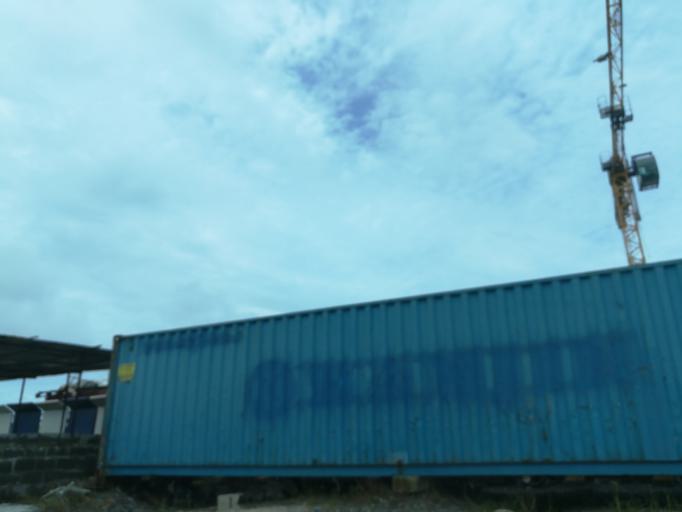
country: NG
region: Lagos
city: Lagos
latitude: 6.4016
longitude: 3.4069
